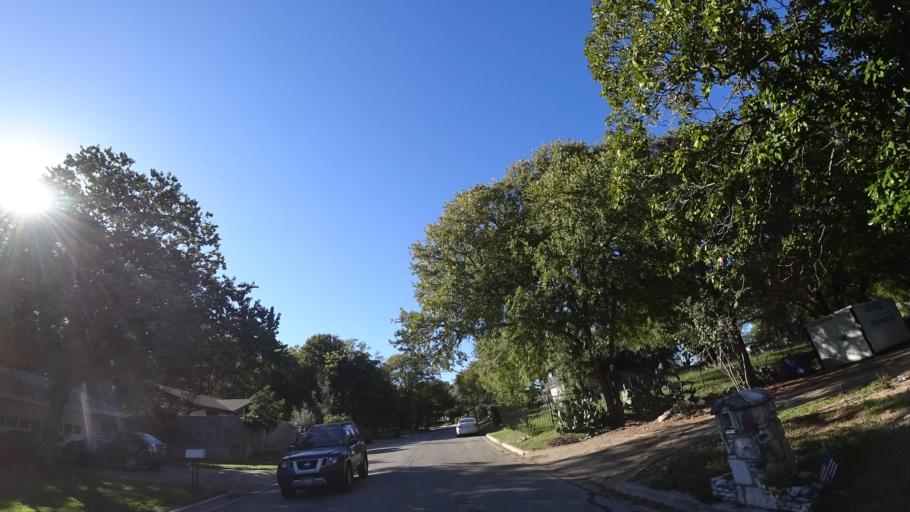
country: US
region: Texas
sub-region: Travis County
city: Austin
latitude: 30.2360
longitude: -97.7306
